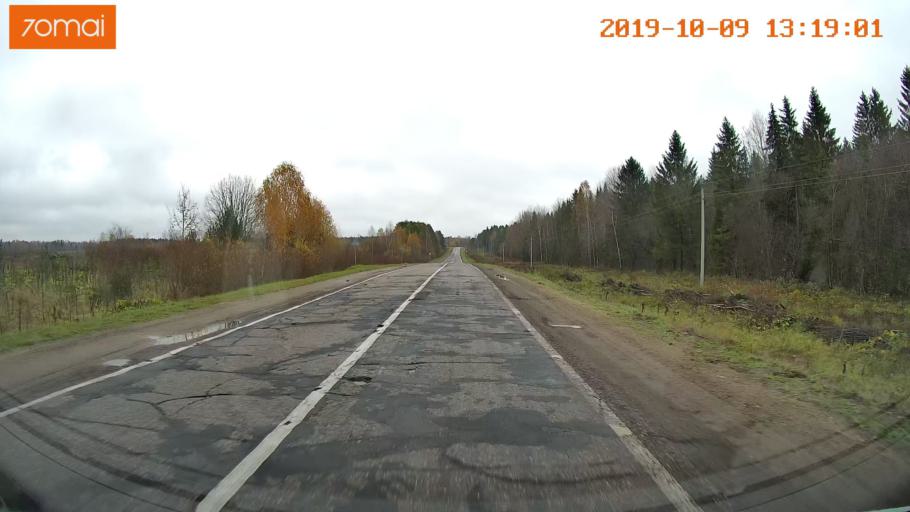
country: RU
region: Jaroslavl
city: Lyubim
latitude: 58.3500
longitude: 40.8053
